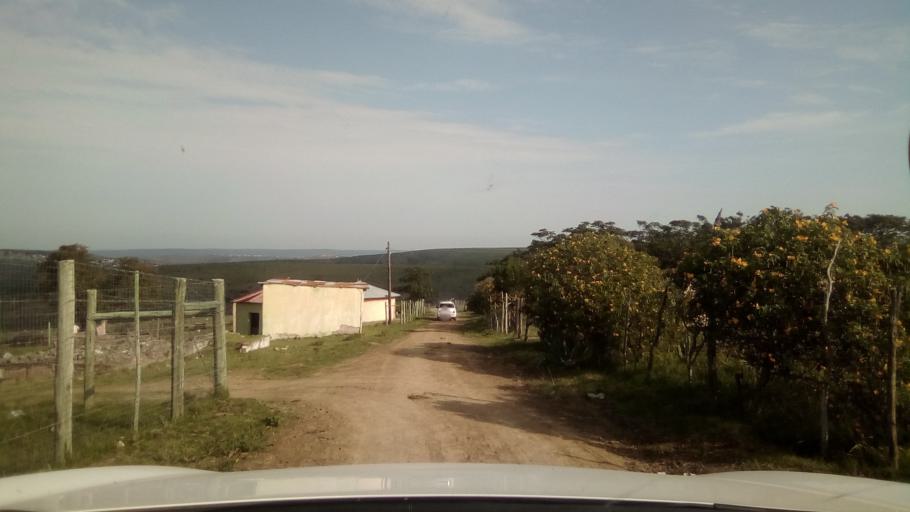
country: ZA
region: Eastern Cape
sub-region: Buffalo City Metropolitan Municipality
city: Bhisho
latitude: -33.0069
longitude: 27.3016
